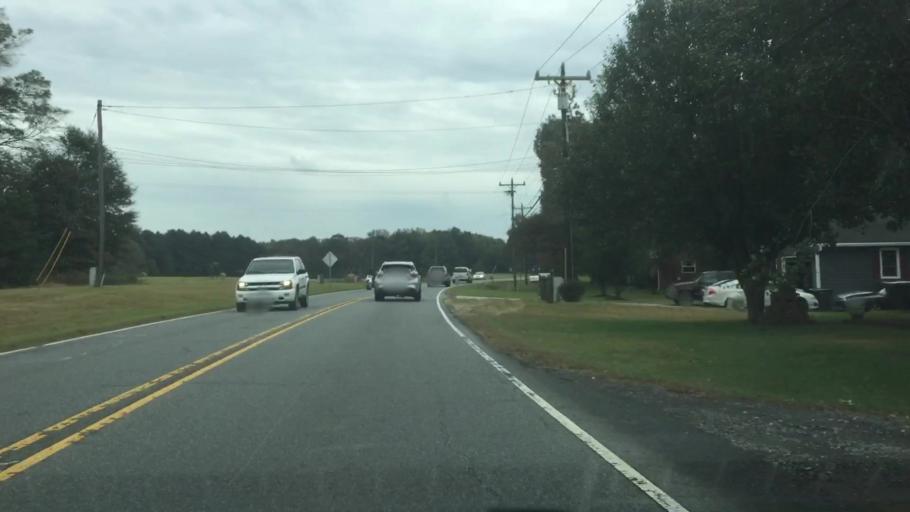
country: US
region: North Carolina
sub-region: Iredell County
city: Mooresville
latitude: 35.6336
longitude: -80.8256
